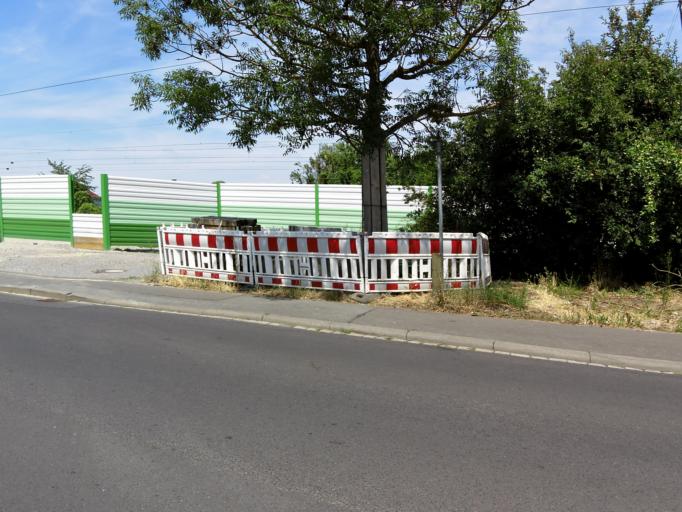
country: DE
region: Bavaria
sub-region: Regierungsbezirk Unterfranken
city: Wuerzburg
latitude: 49.7614
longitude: 9.9487
